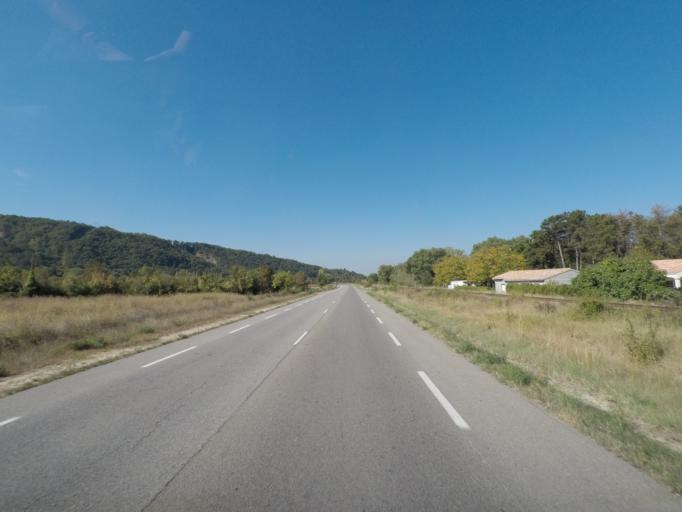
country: FR
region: Rhone-Alpes
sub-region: Departement de la Drome
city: Aouste-sur-Sye
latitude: 44.7137
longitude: 5.0485
